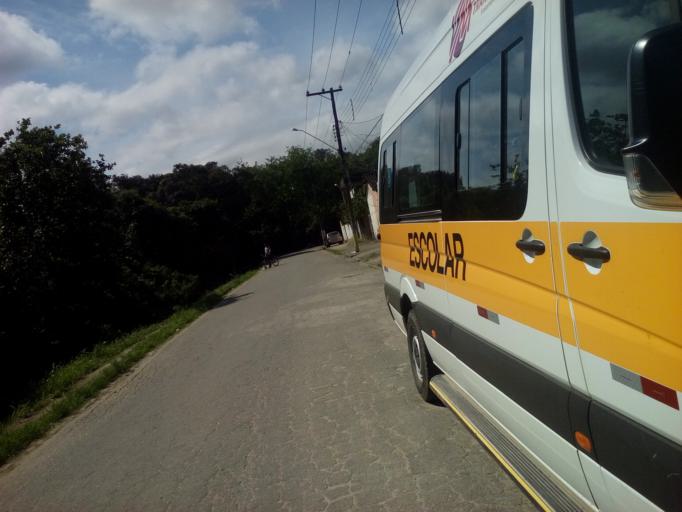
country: BR
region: Sao Paulo
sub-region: Guaruja
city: Guaruja
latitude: -23.9642
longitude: -46.2606
